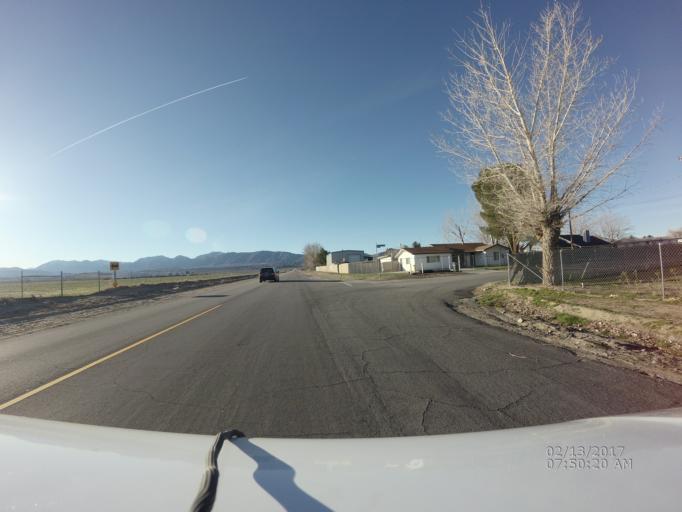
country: US
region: California
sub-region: Los Angeles County
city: Littlerock
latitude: 34.5322
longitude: -117.9582
